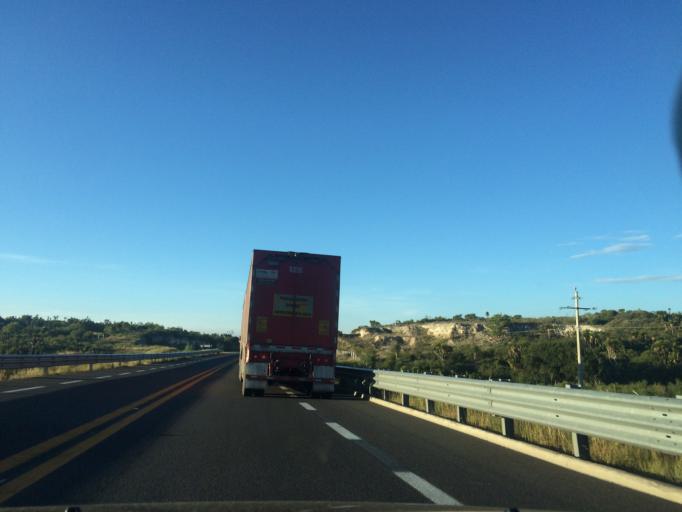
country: MX
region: Puebla
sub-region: Tehuacan
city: Magdalena Cuayucatepec
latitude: 18.5792
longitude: -97.4652
